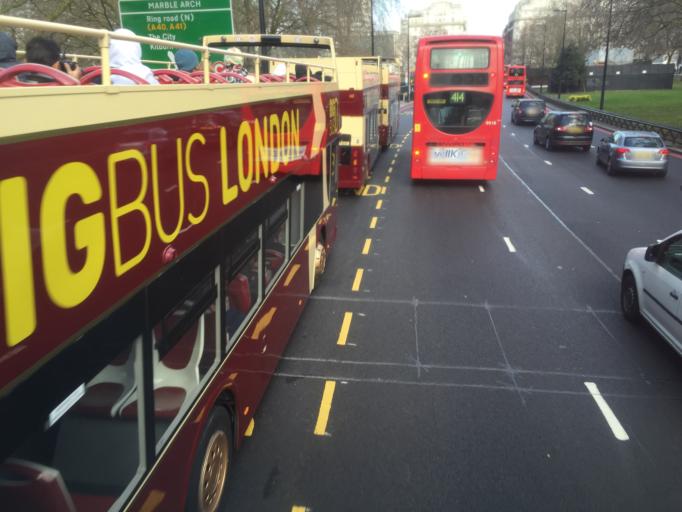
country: GB
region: England
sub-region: Greater London
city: Chelsea
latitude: 51.5110
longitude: -0.1578
